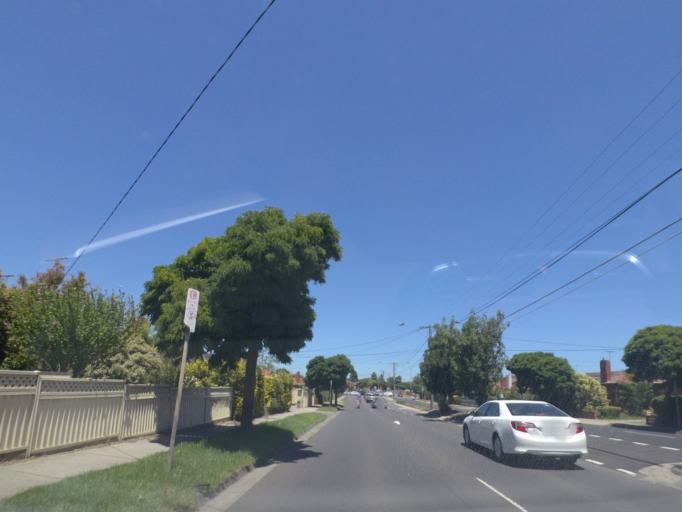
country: AU
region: Victoria
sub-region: Darebin
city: Preston
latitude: -37.7389
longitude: 145.0237
